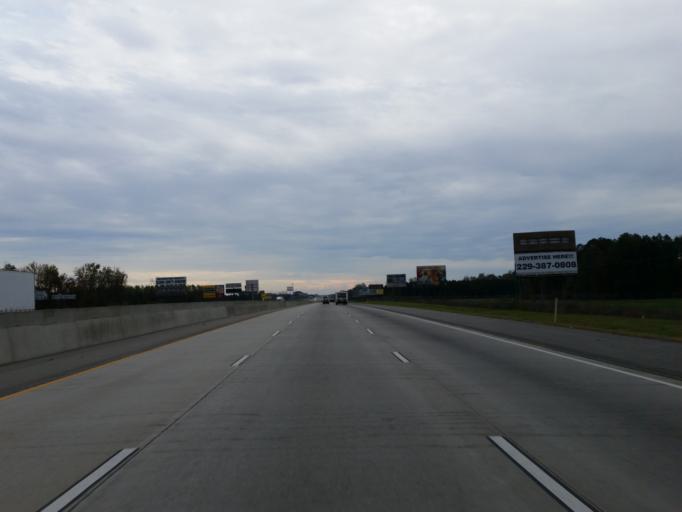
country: US
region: Georgia
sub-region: Tift County
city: Unionville
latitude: 31.3983
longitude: -83.5002
